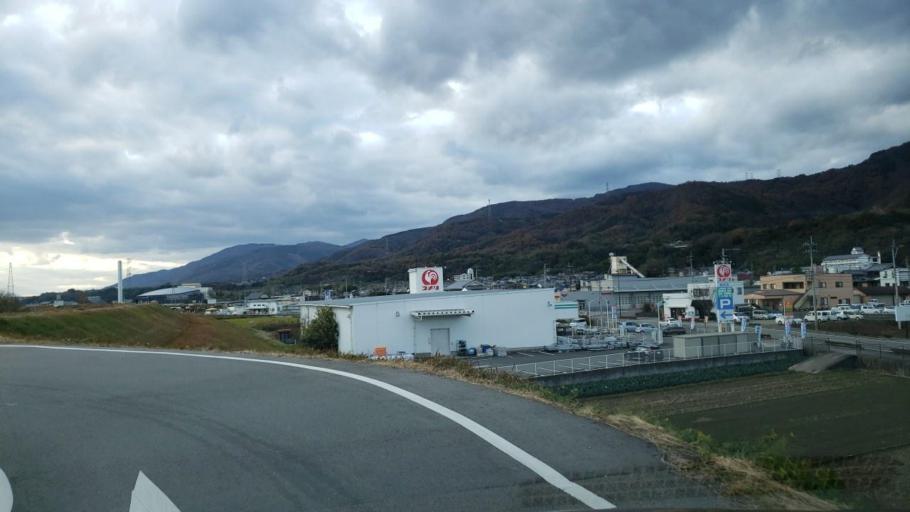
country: JP
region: Tokushima
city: Wakimachi
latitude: 34.0677
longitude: 134.1424
